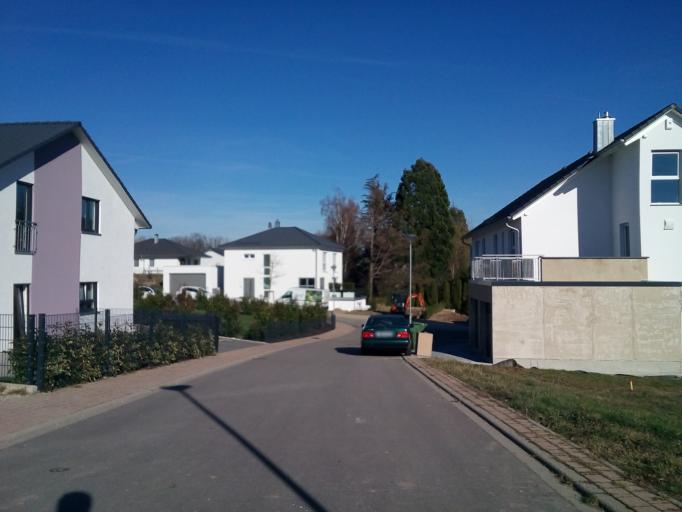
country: DE
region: Baden-Wuerttemberg
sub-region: Freiburg Region
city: Achern
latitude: 48.6240
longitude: 8.0629
